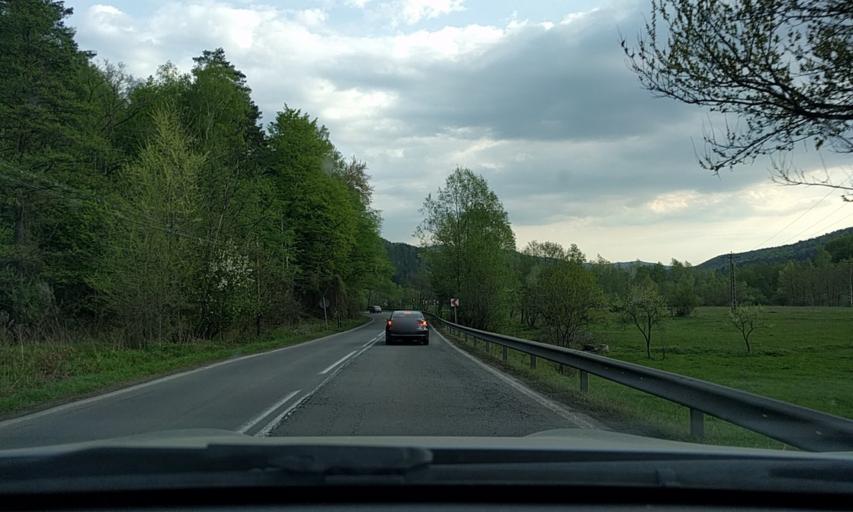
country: RO
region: Bacau
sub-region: Oras Slanic-Moldova
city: Slanic-Moldova
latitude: 46.1552
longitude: 26.4602
